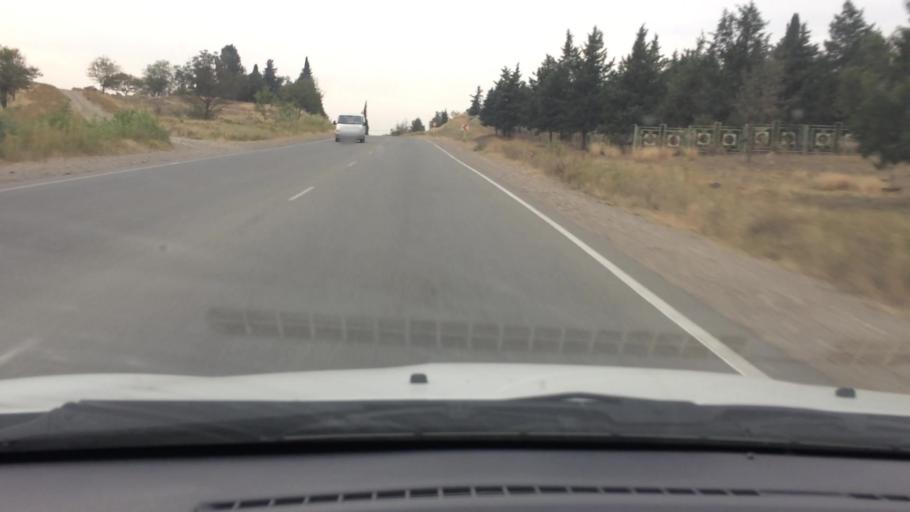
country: GE
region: Kvemo Kartli
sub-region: Marneuli
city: Marneuli
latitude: 41.5253
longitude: 44.7773
